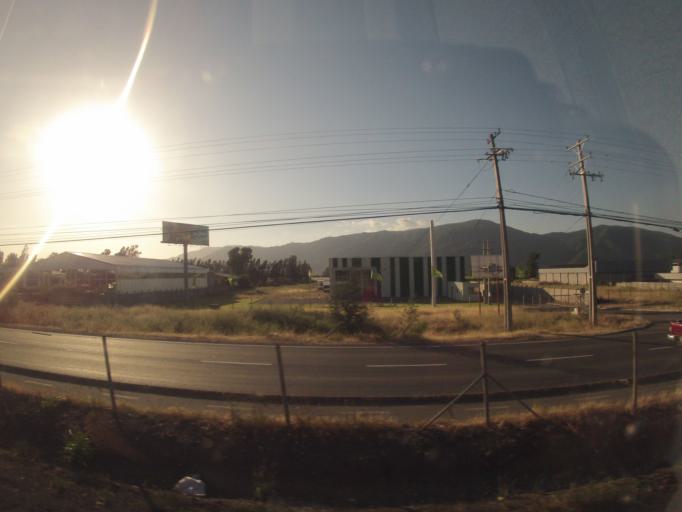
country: CL
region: O'Higgins
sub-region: Provincia de Colchagua
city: Chimbarongo
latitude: -34.5668
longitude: -70.9700
